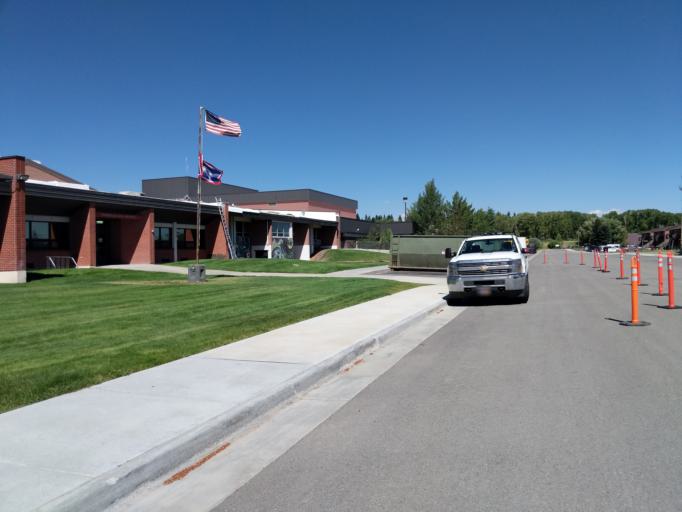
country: US
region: Wyoming
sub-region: Sublette County
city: Pinedale
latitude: 42.8702
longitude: -109.8602
